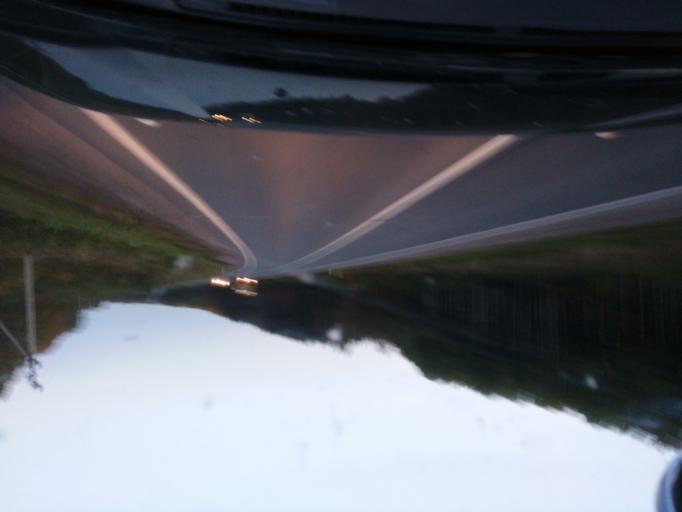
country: RU
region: Perm
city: Verkhnechusovskiye Gorodki
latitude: 58.2380
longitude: 57.2210
